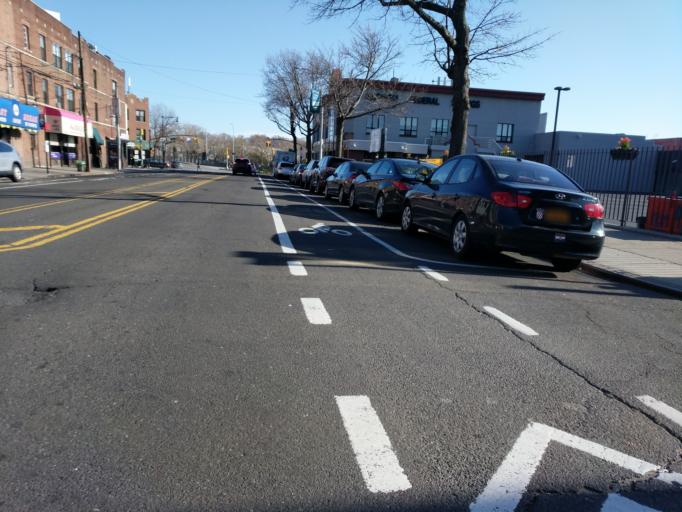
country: US
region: New York
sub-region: Queens County
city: Long Island City
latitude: 40.7268
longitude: -73.8955
